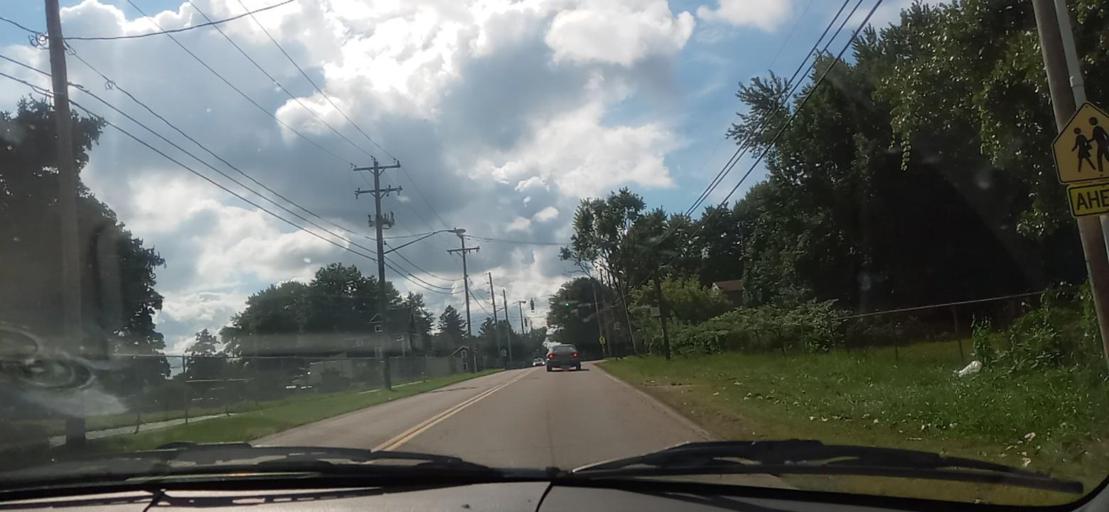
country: US
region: Ohio
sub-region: Summit County
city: Barberton
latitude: 41.0325
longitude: -81.5653
